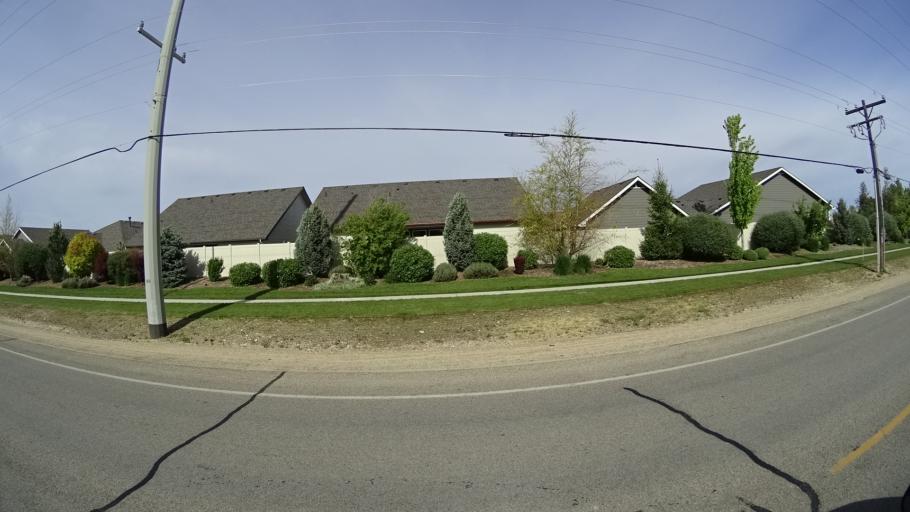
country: US
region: Idaho
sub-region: Ada County
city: Meridian
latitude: 43.5633
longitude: -116.3344
